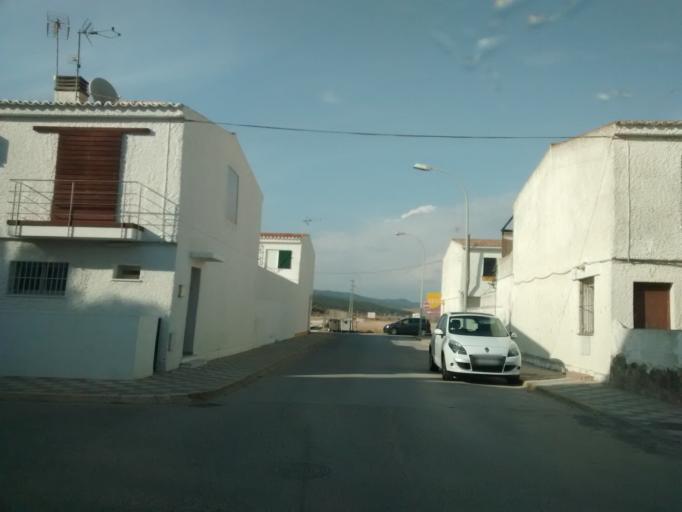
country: ES
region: Andalusia
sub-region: Provincia de Cadiz
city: Zahara de los Atunes
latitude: 36.1353
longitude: -5.8424
